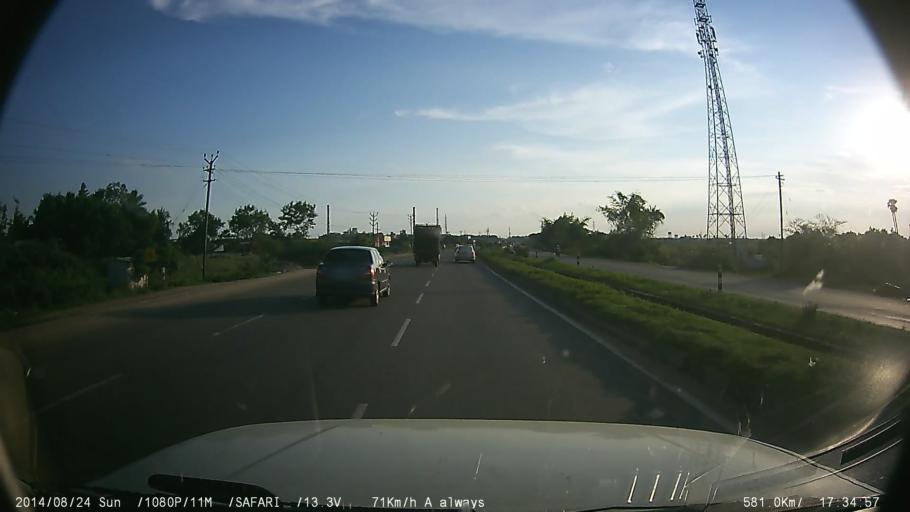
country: IN
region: Tamil Nadu
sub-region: Kancheepuram
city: Sriperumbudur
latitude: 12.9459
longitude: 79.9234
